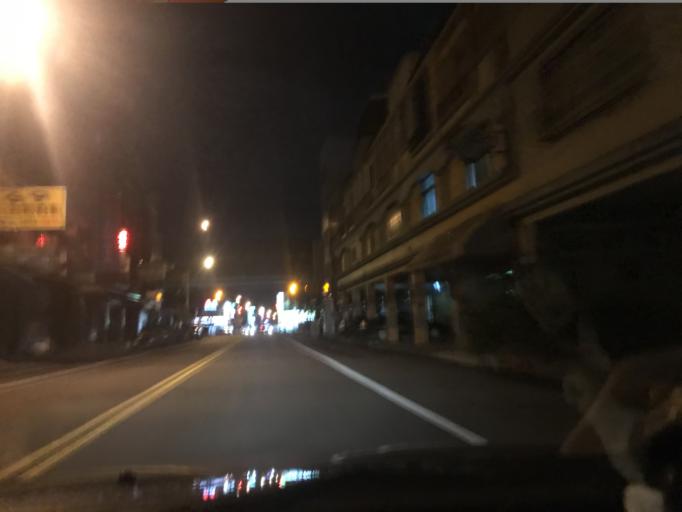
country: TW
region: Taiwan
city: Daxi
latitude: 24.8582
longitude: 121.2146
